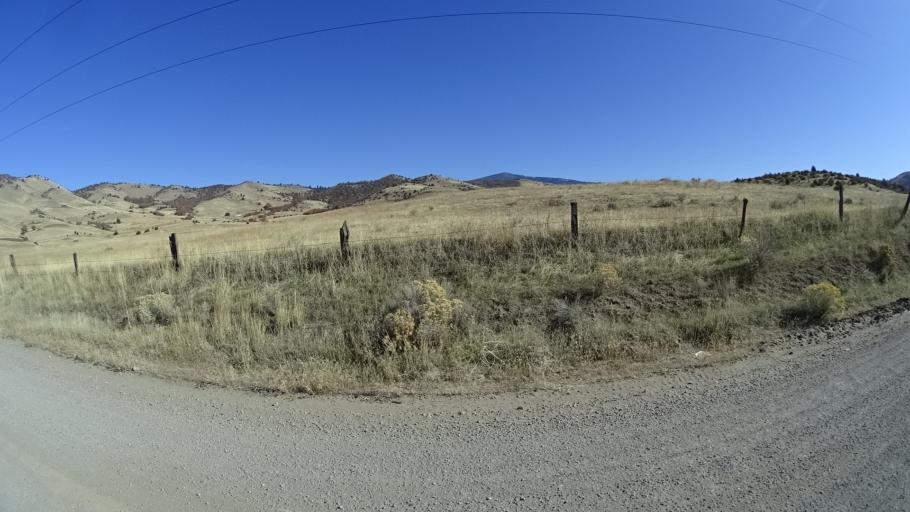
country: US
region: California
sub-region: Siskiyou County
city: Montague
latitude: 41.8249
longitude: -122.3623
